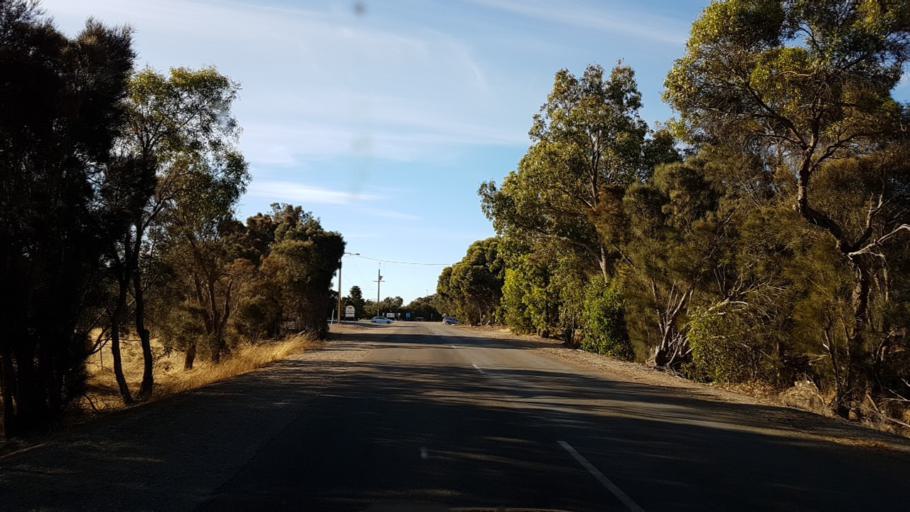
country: AU
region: South Australia
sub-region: Yorke Peninsula
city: Port Victoria
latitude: -34.9270
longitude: 137.0845
